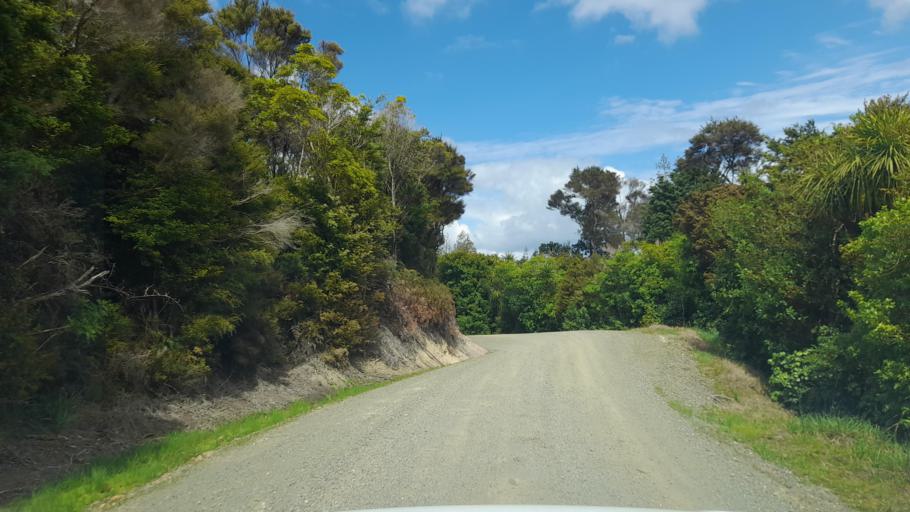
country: NZ
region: Auckland
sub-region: Auckland
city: Wellsford
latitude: -36.2055
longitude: 174.3364
